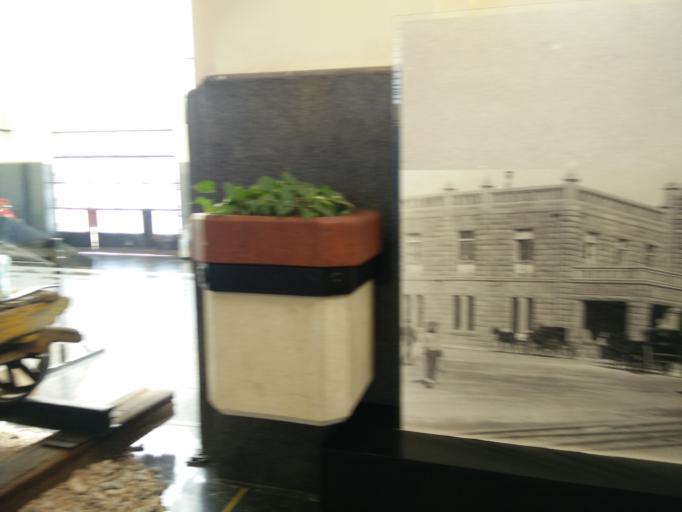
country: MX
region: San Luis Potosi
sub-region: San Luis Potosi
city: San Luis Potosi
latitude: 22.1530
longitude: -100.9715
